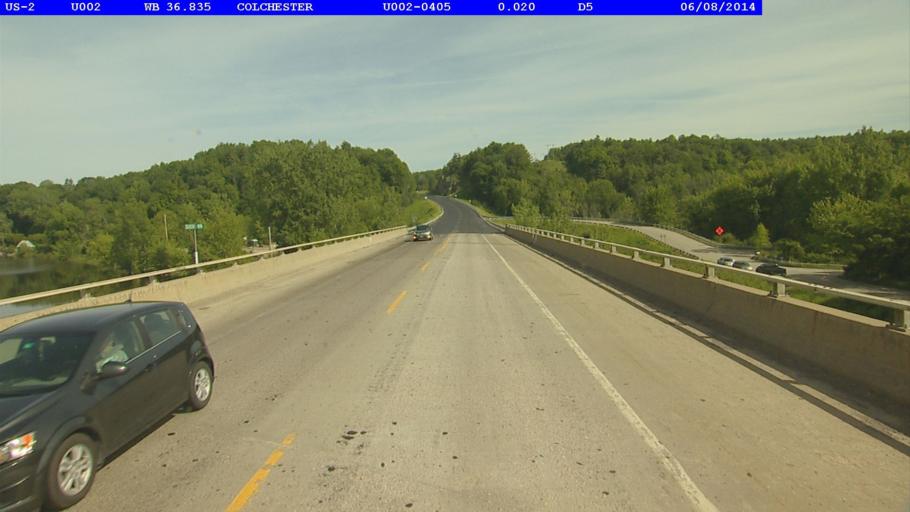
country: US
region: Vermont
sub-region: Chittenden County
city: Colchester
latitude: 44.6033
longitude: -73.2046
